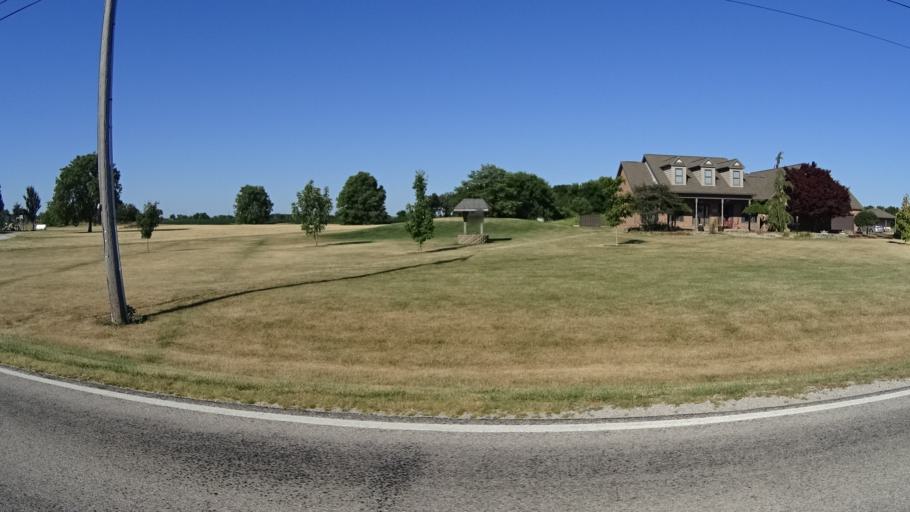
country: US
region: Ohio
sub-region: Erie County
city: Sandusky
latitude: 41.3676
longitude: -82.7631
